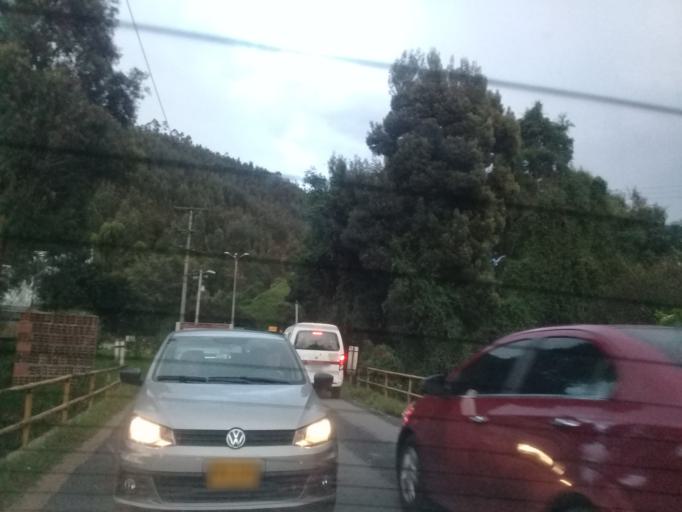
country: CO
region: Cundinamarca
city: Tabio
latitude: 4.9261
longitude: -74.0683
